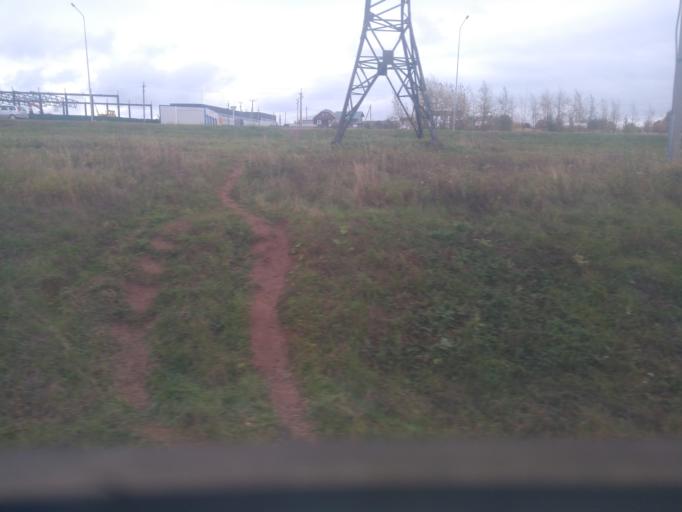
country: RU
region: Tatarstan
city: Mendeleyevsk
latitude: 55.8857
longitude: 52.3131
